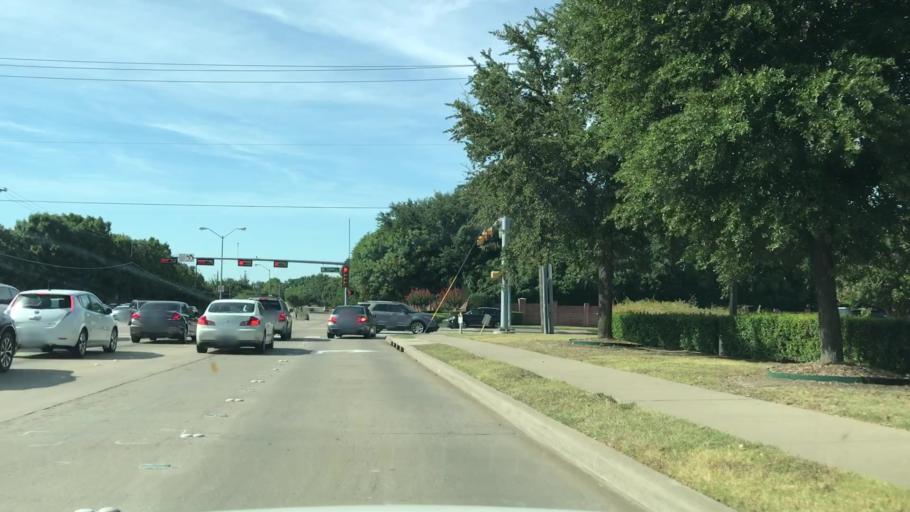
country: US
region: Texas
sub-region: Denton County
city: The Colony
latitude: 33.0457
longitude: -96.8396
